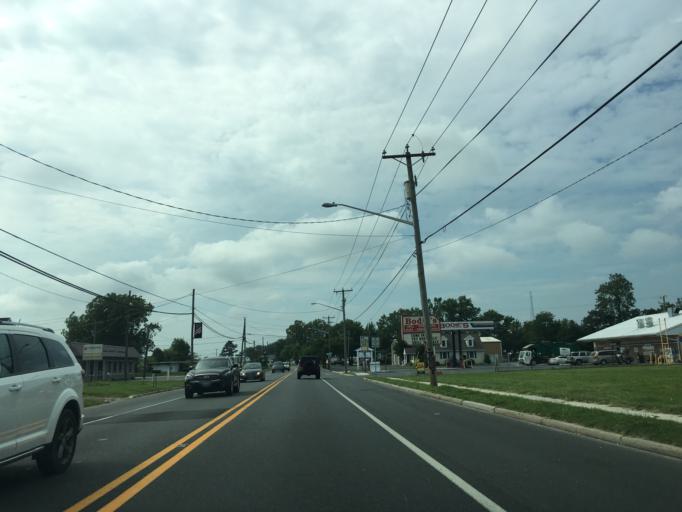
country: US
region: Delaware
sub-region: Sussex County
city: Millsboro
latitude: 38.5519
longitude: -75.2477
